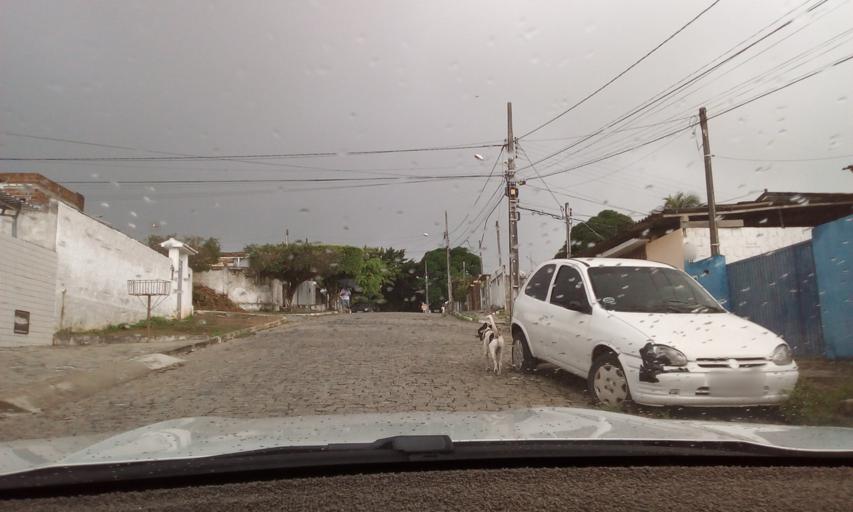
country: BR
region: Paraiba
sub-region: Bayeux
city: Bayeux
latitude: -7.1587
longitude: -34.9017
